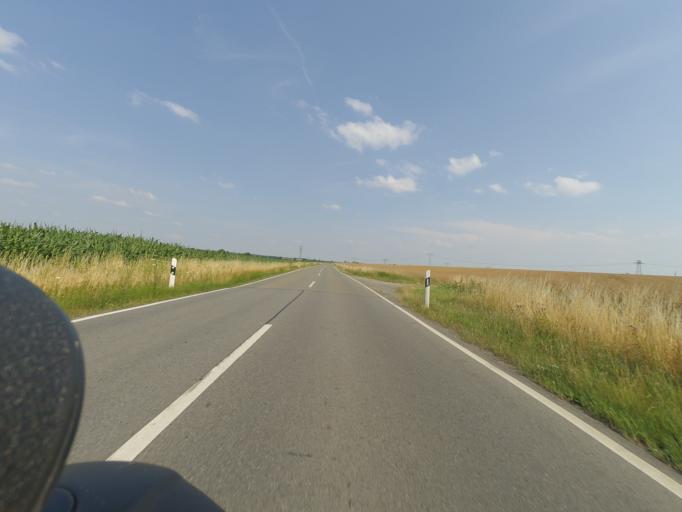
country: DE
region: Thuringia
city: Gerstenberg
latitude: 51.0279
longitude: 12.4458
